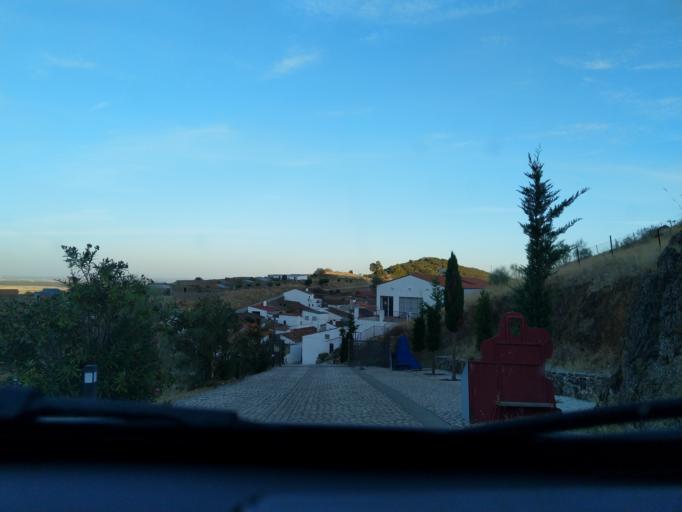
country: ES
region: Extremadura
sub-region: Provincia de Badajoz
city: Reina
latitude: 38.1867
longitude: -5.9501
